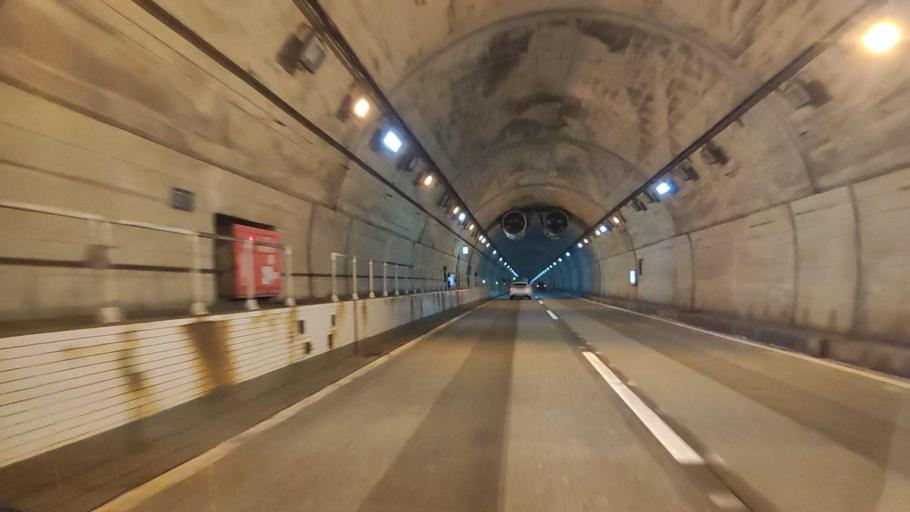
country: JP
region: Iwate
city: Ichinohe
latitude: 40.2306
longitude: 141.3760
